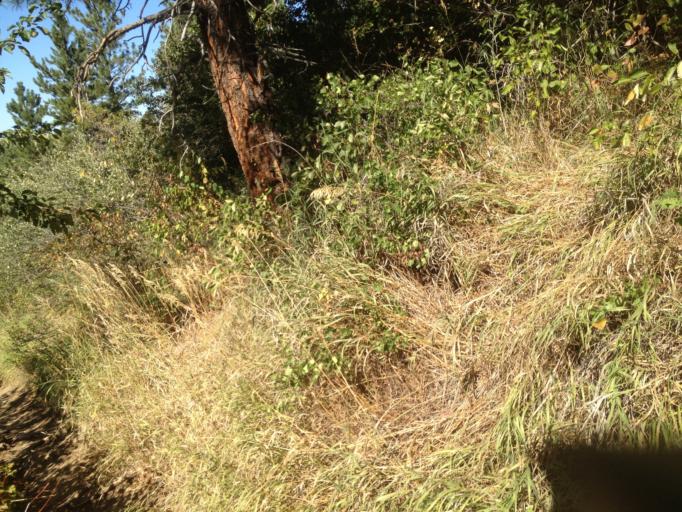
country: US
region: Colorado
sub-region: Boulder County
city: Boulder
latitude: 39.9944
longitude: -105.2817
